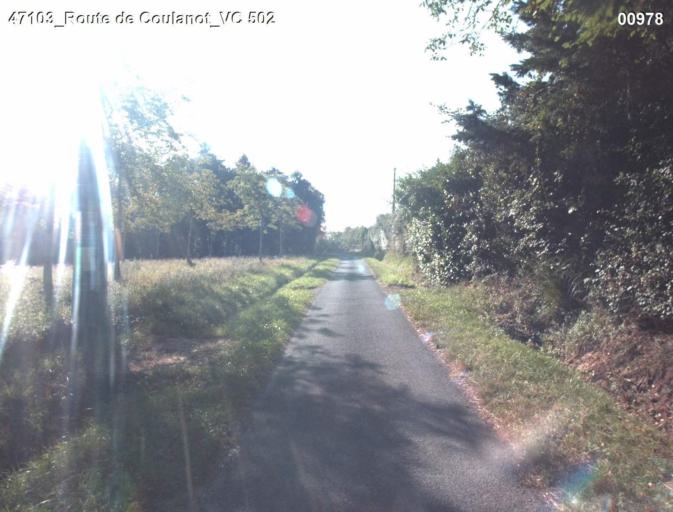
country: FR
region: Aquitaine
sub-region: Departement du Lot-et-Garonne
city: Nerac
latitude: 44.0722
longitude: 0.3398
